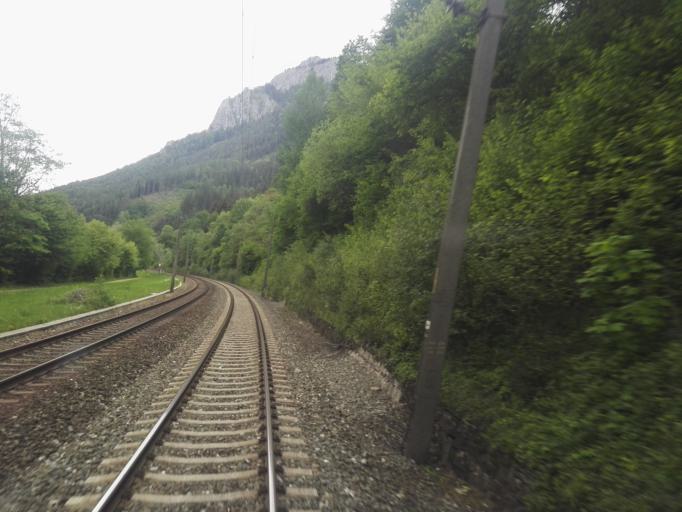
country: AT
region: Styria
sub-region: Politischer Bezirk Graz-Umgebung
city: Rothelstein
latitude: 47.3096
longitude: 15.3784
